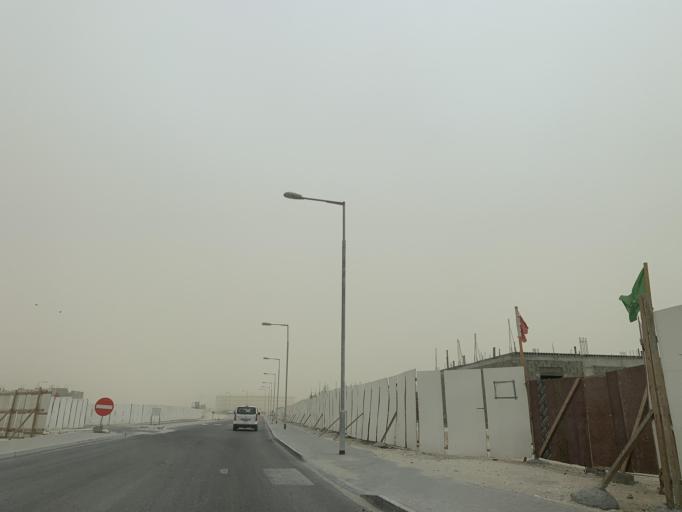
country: BH
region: Central Governorate
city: Madinat Hamad
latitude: 26.1244
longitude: 50.5094
